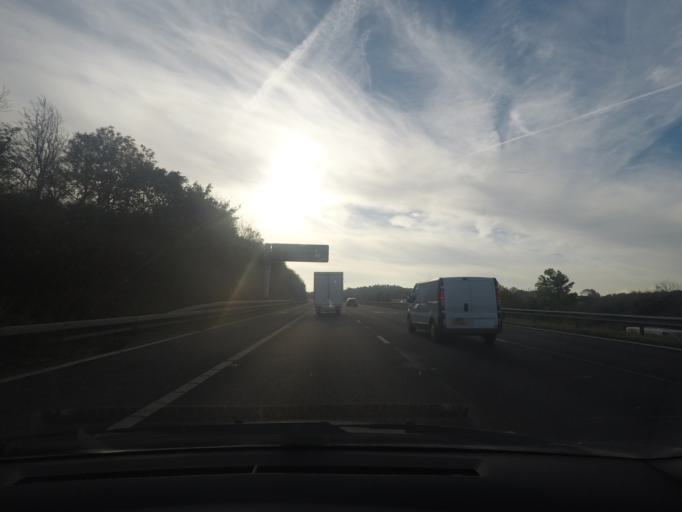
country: GB
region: England
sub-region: Barnsley
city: Dodworth
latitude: 53.5612
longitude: -1.5358
